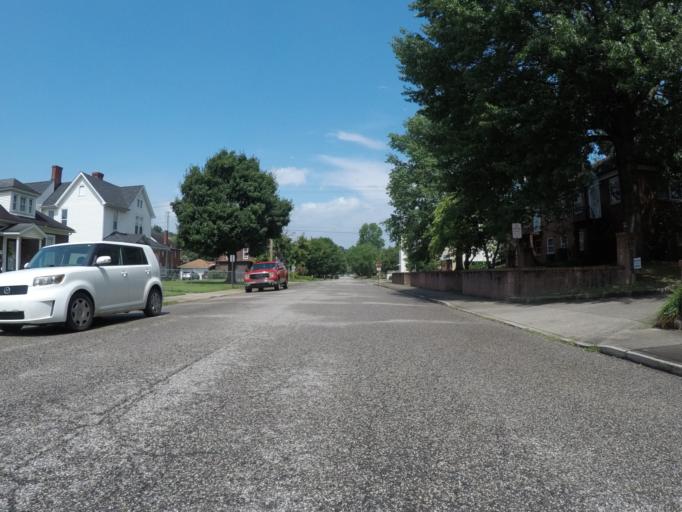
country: US
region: Kentucky
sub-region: Boyd County
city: Ashland
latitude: 38.4753
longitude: -82.6432
